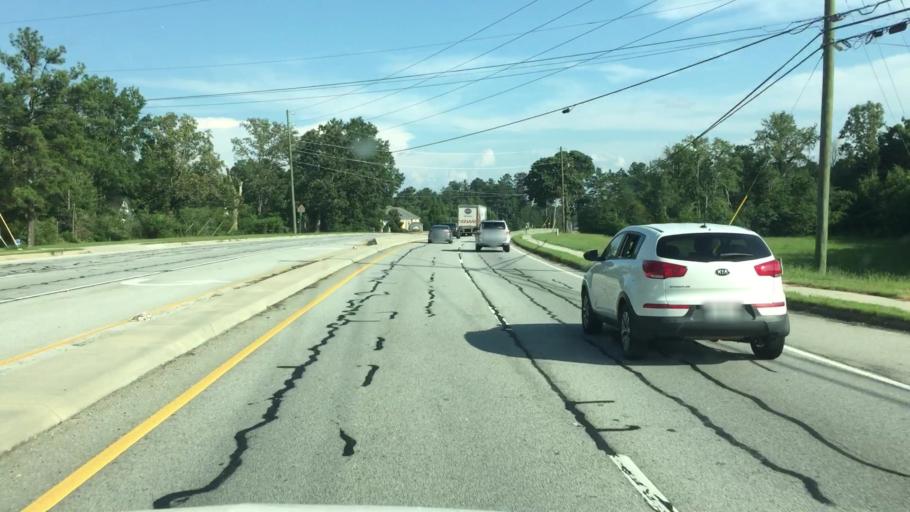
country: US
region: Georgia
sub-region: Gwinnett County
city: Snellville
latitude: 33.8343
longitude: -84.0325
